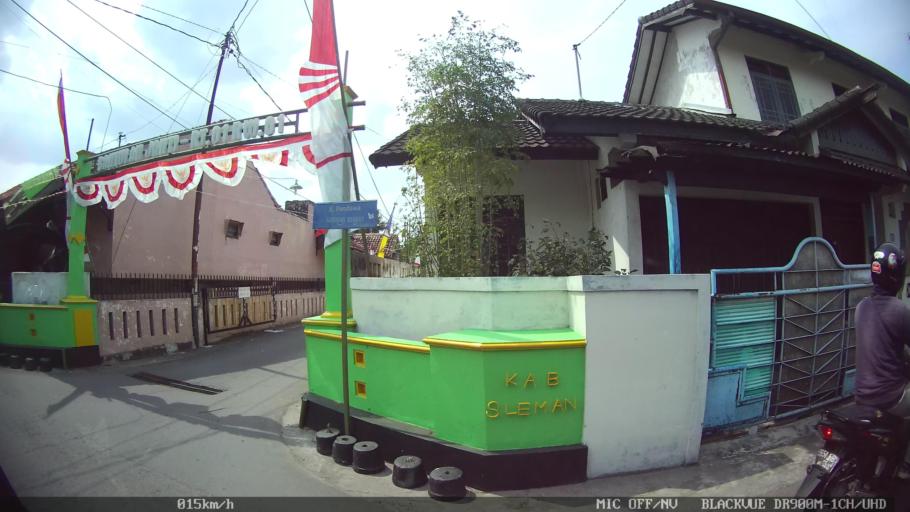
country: ID
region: Daerah Istimewa Yogyakarta
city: Depok
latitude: -7.7850
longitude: 110.4057
